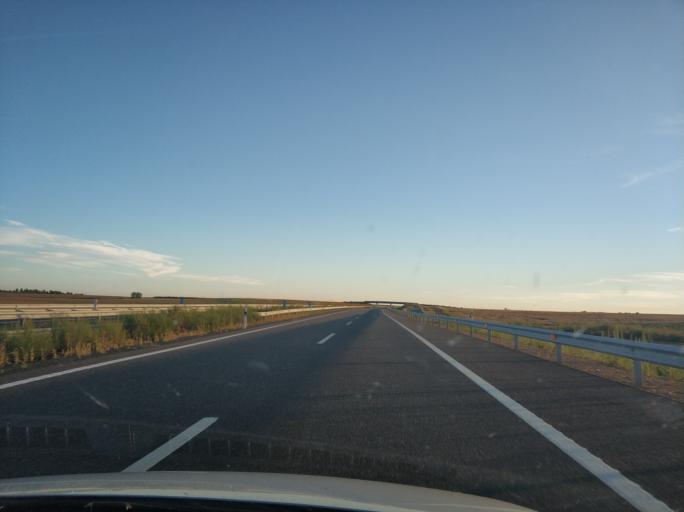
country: ES
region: Castille and Leon
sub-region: Provincia de Zamora
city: Castrogonzalo
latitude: 41.9586
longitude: -5.6134
